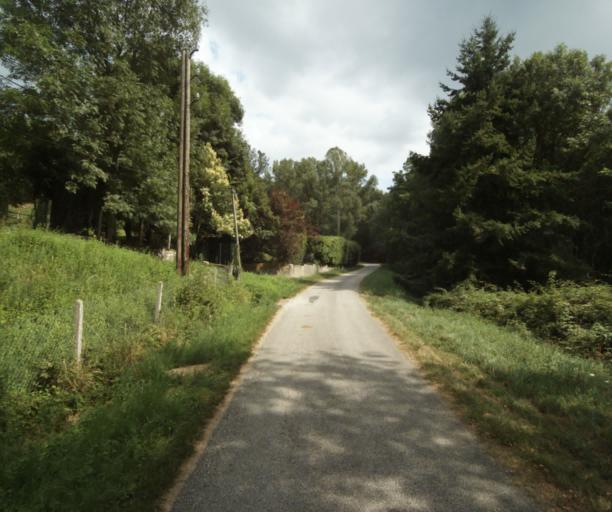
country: FR
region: Midi-Pyrenees
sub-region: Departement du Tarn
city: Soreze
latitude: 43.4326
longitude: 2.0424
